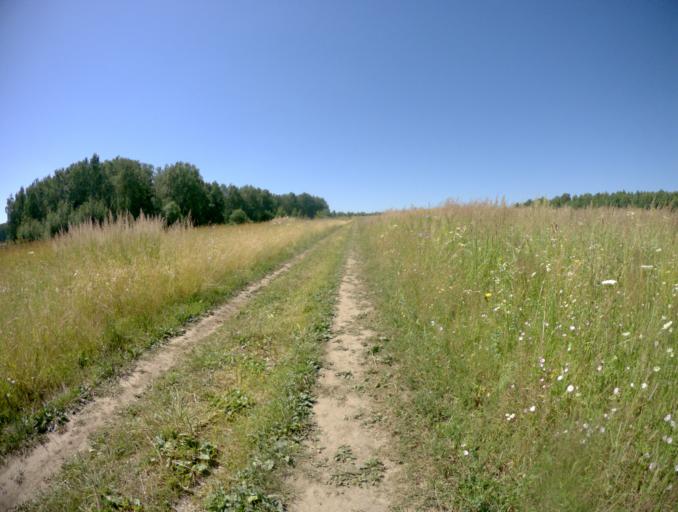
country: RU
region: Nizjnij Novgorod
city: Reshetikha
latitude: 56.1271
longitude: 43.2670
